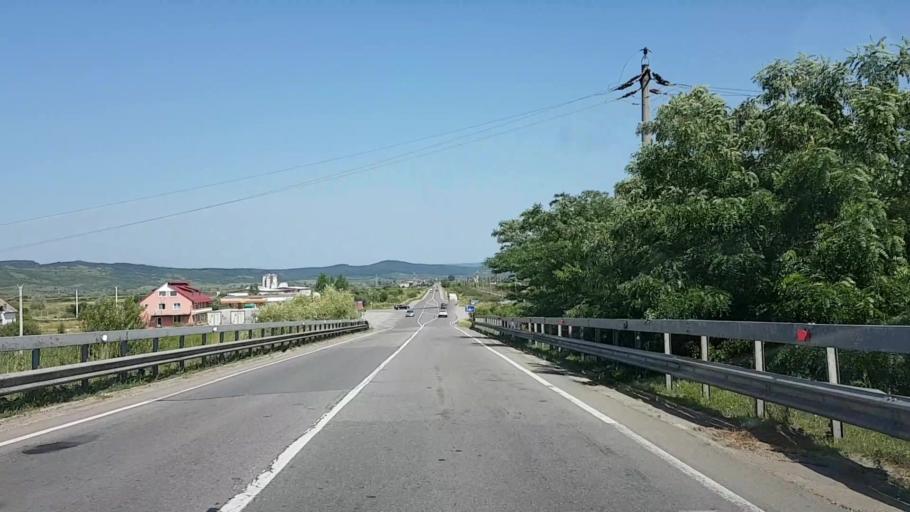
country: RO
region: Bistrita-Nasaud
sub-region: Comuna Sintereag
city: Cociu
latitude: 47.1826
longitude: 24.2360
